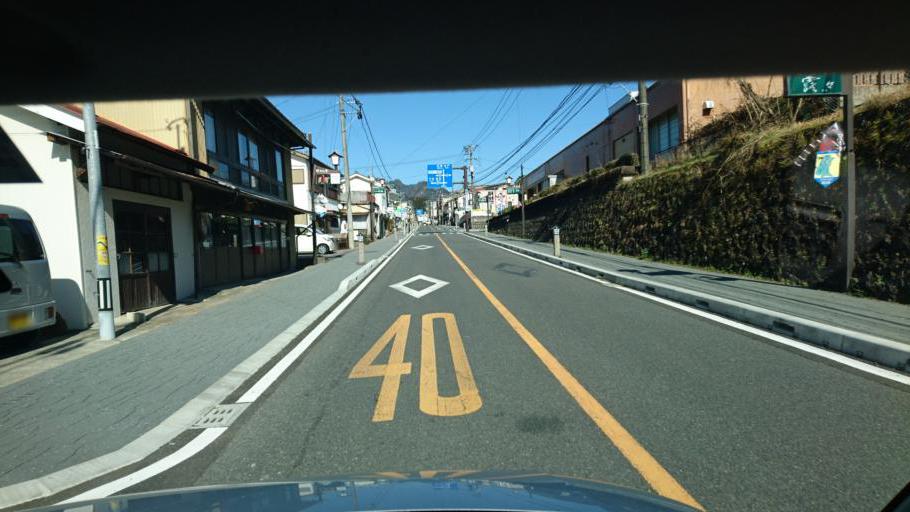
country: JP
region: Oita
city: Takedamachi
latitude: 32.7079
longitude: 131.3051
